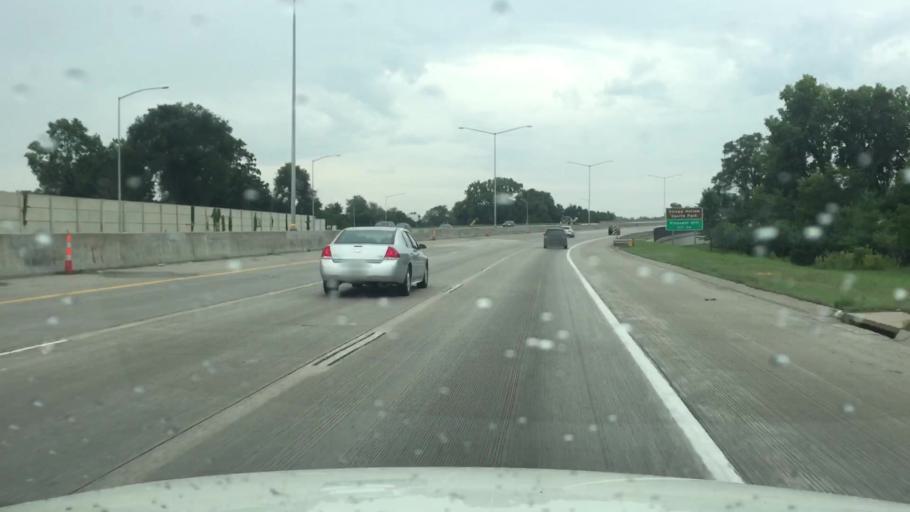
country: US
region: Iowa
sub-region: Polk County
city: Des Moines
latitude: 41.6074
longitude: -93.5791
